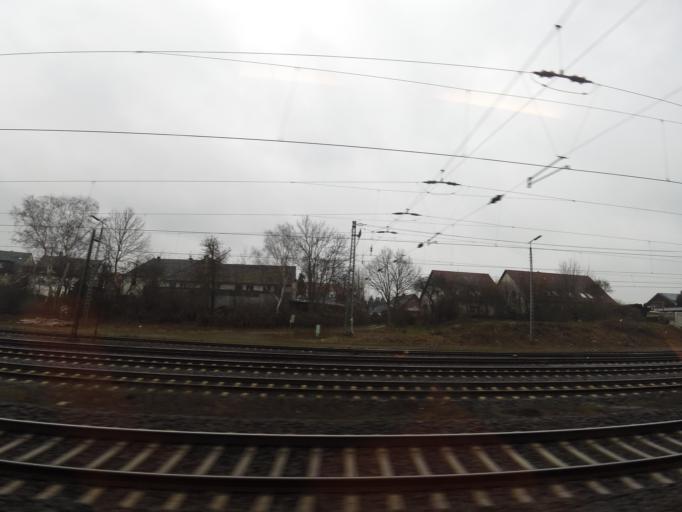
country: DE
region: North Rhine-Westphalia
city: Loehne
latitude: 52.1981
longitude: 8.7224
